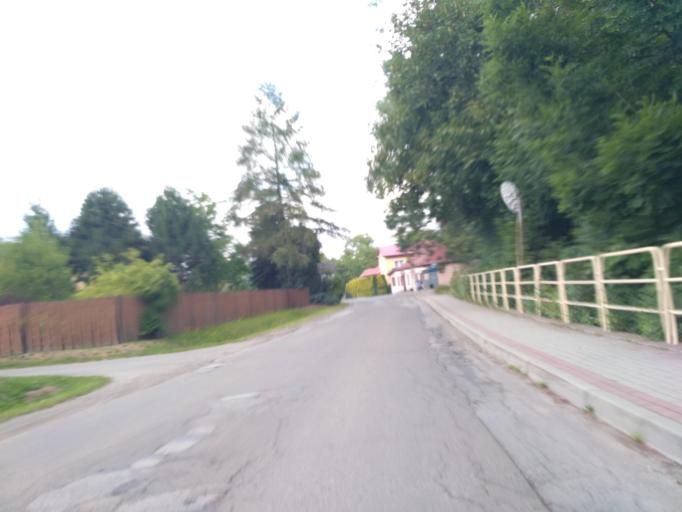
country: PL
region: Subcarpathian Voivodeship
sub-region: Powiat krosnienski
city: Iwonicz-Zdroj
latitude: 49.5777
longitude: 21.7525
